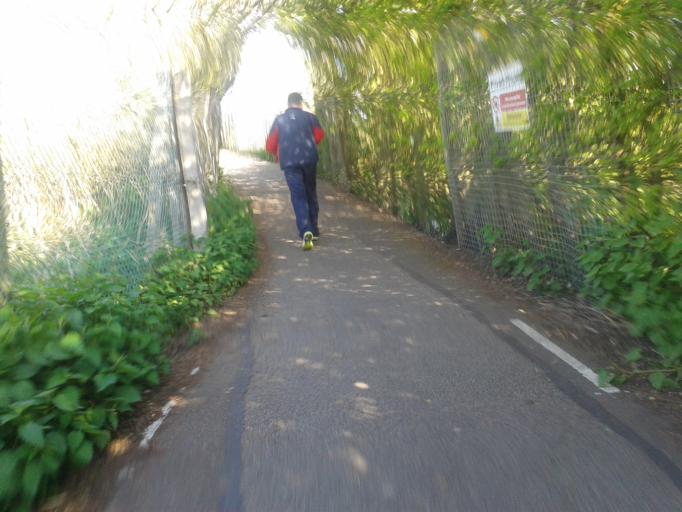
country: GB
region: England
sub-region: Cambridgeshire
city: Cambridge
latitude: 52.1953
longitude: 0.1624
